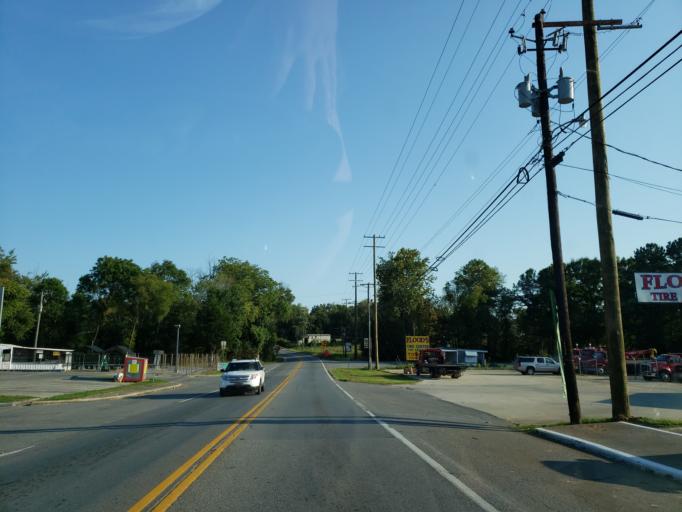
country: US
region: Georgia
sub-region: Murray County
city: Chatsworth
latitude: 34.7618
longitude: -84.8222
